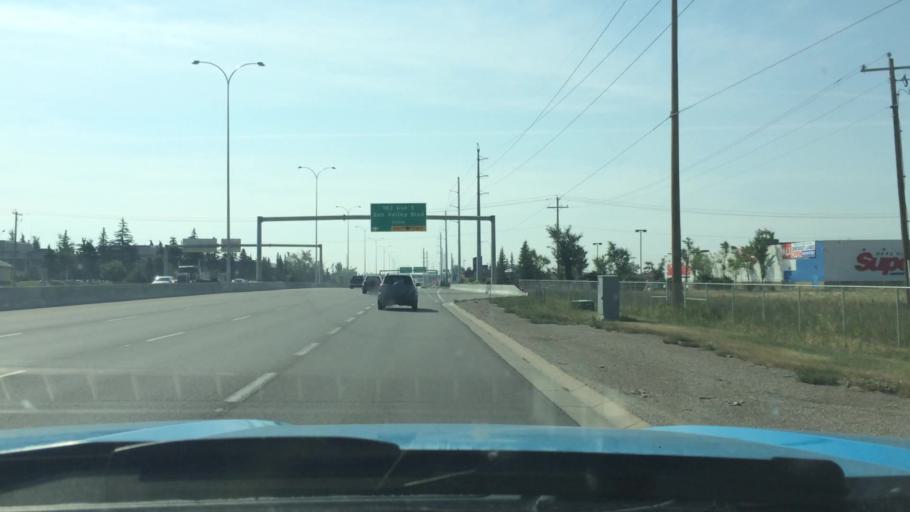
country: CA
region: Alberta
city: Calgary
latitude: 50.9119
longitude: -114.0668
